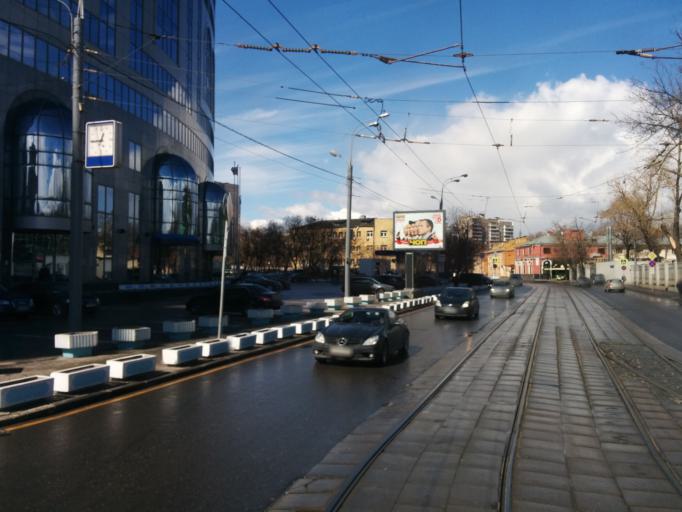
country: RU
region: Moscow
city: Sokol'niki
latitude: 55.7766
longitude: 37.6490
